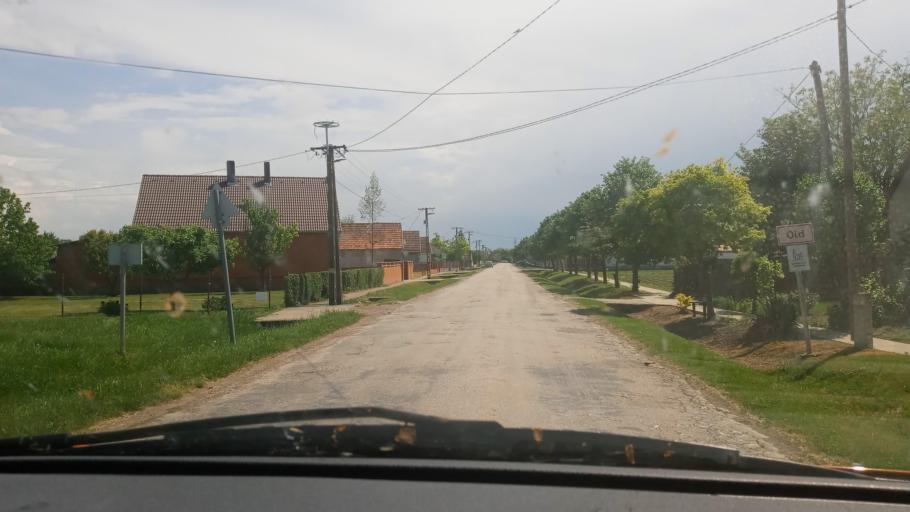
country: HU
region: Baranya
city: Siklos
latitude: 45.7945
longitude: 18.3502
